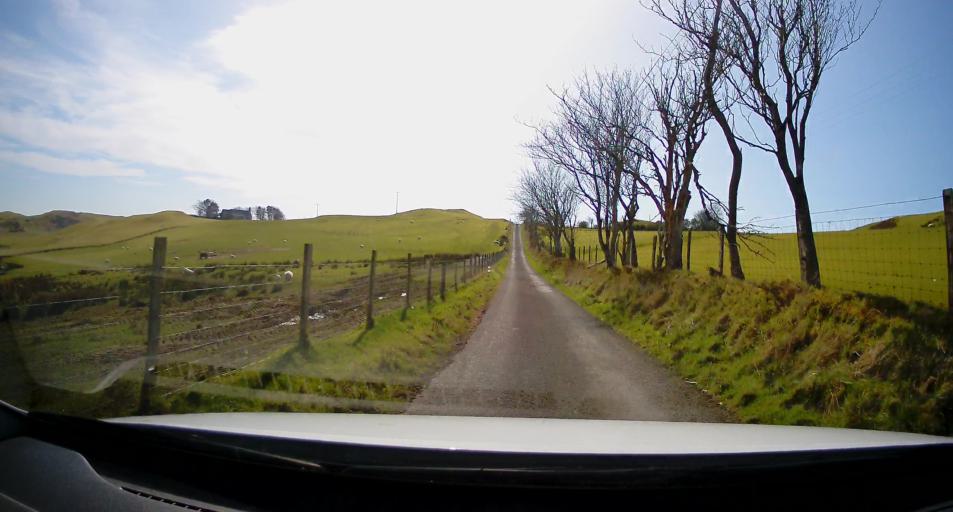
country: GB
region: Wales
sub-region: County of Ceredigion
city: Lledrod
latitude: 52.3616
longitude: -3.8707
